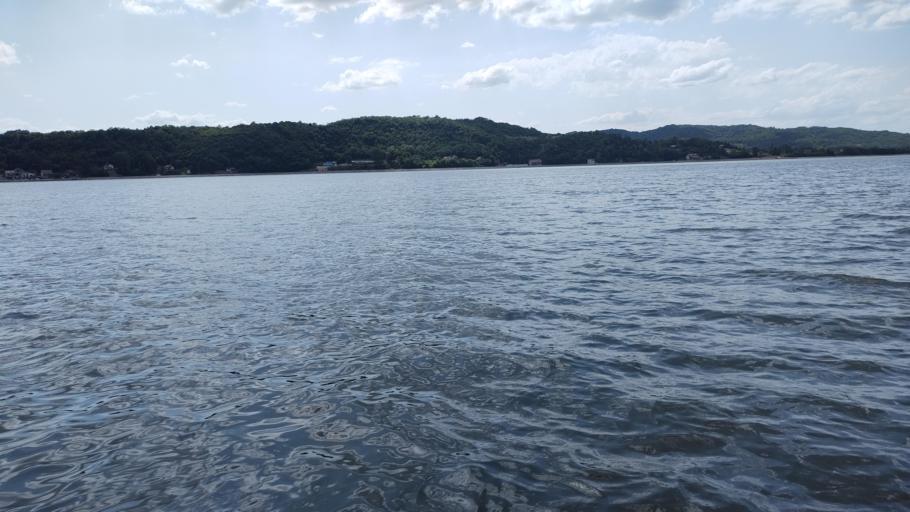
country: RS
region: Central Serbia
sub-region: Branicevski Okrug
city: Golubac
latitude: 44.6618
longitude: 21.6291
